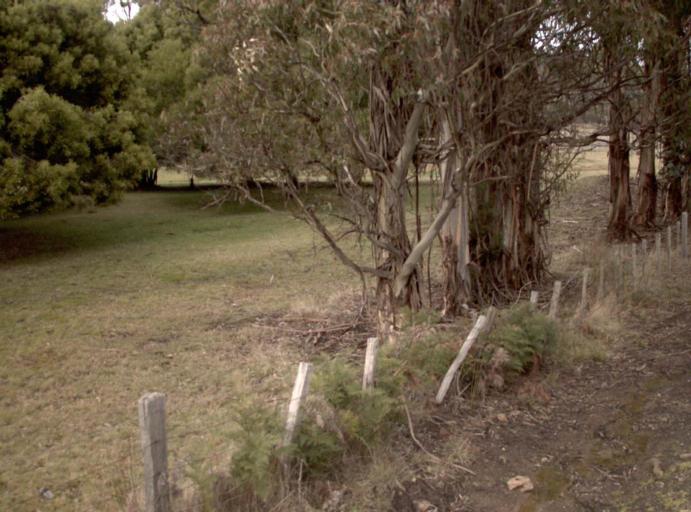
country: AU
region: Tasmania
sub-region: Launceston
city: Newstead
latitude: -41.4117
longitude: 147.2878
